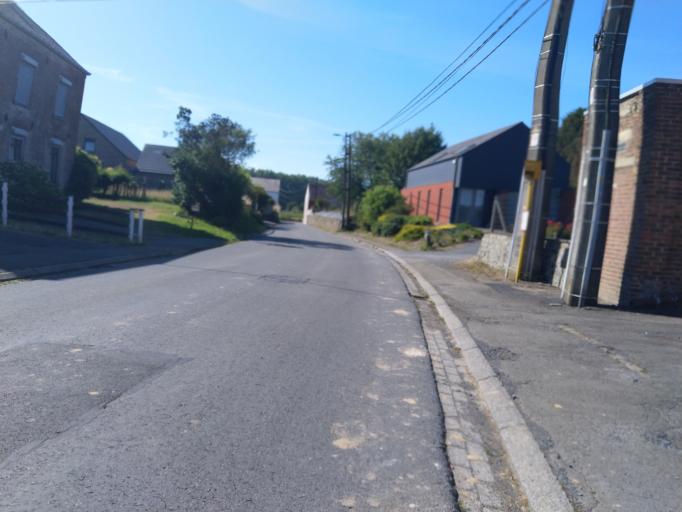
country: BE
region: Wallonia
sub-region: Province du Hainaut
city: Quevy-le-Petit
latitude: 50.3435
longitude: 3.9459
